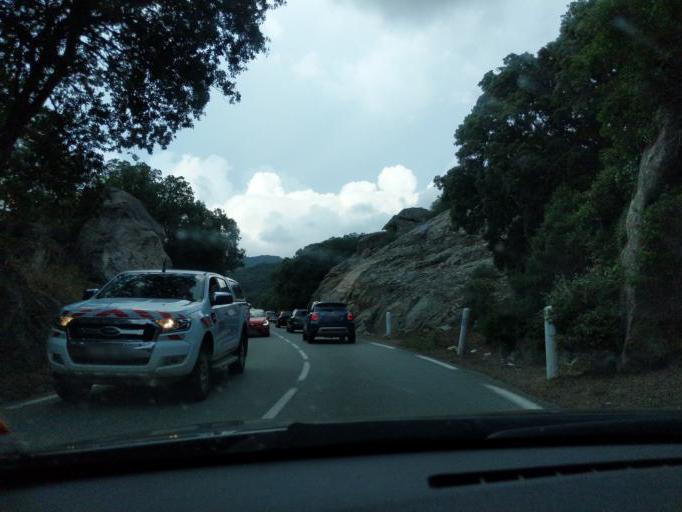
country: FR
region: Corsica
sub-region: Departement de la Corse-du-Sud
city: Sartene
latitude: 41.5810
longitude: 8.9393
